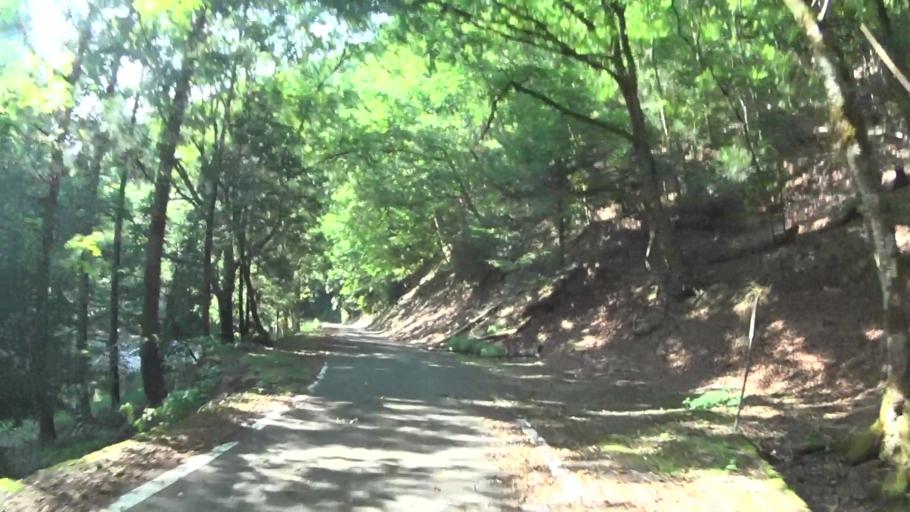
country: JP
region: Fukui
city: Obama
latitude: 35.2702
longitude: 135.6960
